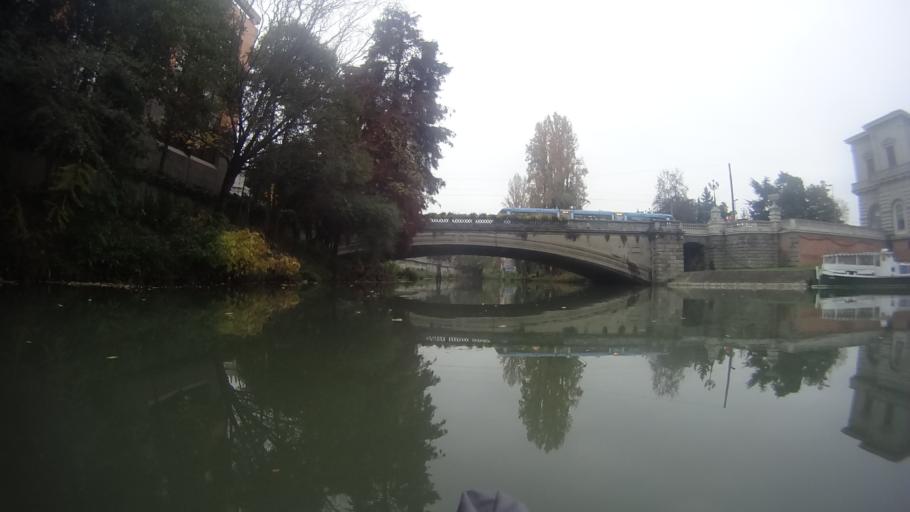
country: IT
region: Veneto
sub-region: Provincia di Padova
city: Padova
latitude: 45.4135
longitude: 11.8783
